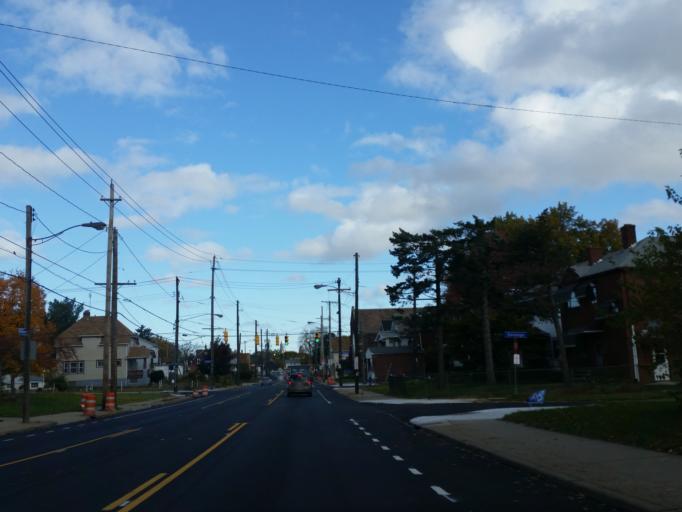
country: US
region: Ohio
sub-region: Cuyahoga County
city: Brooklyn Heights
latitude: 41.4318
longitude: -81.6972
